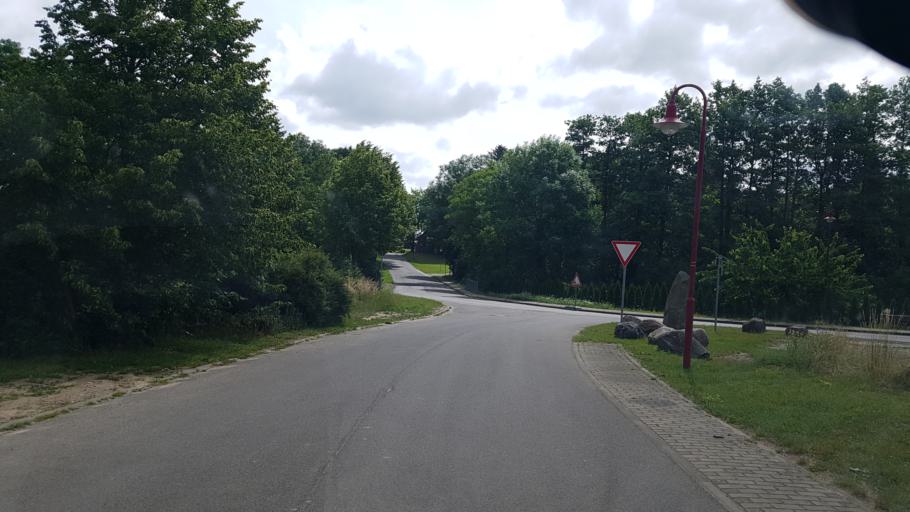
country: DE
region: Mecklenburg-Vorpommern
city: Strasburg
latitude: 53.4364
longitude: 13.7083
